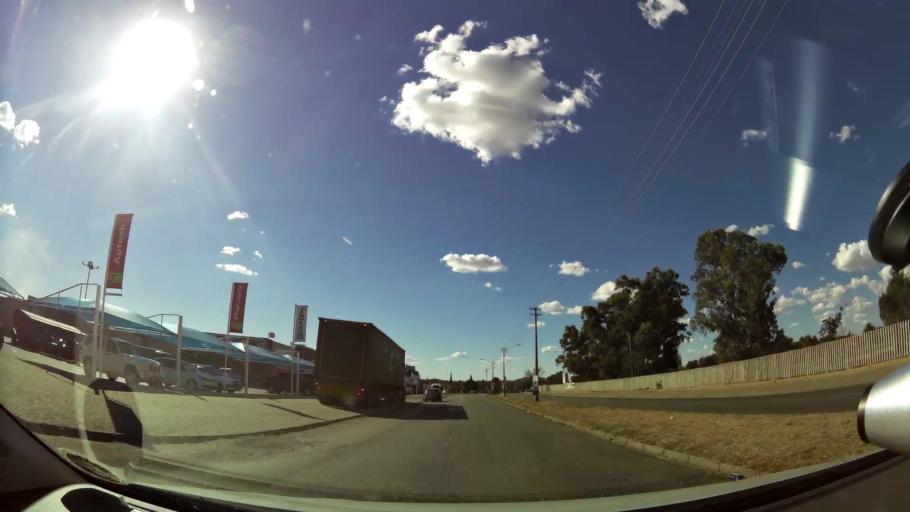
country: ZA
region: North-West
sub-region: Dr Kenneth Kaunda District Municipality
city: Klerksdorp
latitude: -26.8587
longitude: 26.6433
